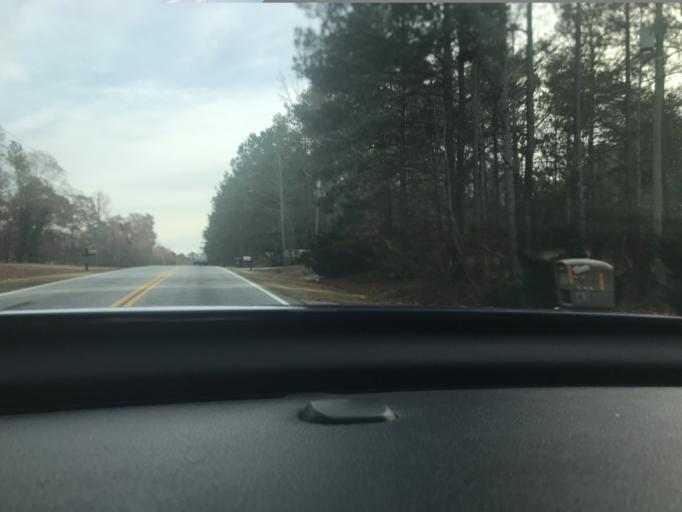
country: US
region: Georgia
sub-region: Newton County
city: Porterdale
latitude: 33.5946
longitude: -83.9148
